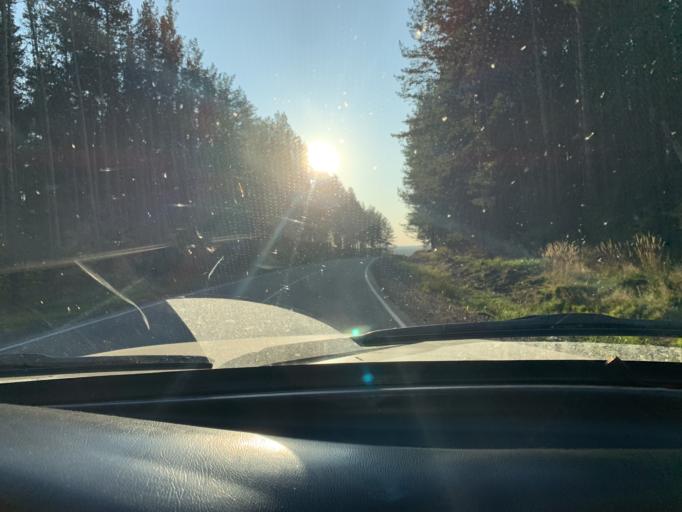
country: RU
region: Sverdlovsk
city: Verkhneye Dubrovo
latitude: 56.8671
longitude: 61.0697
